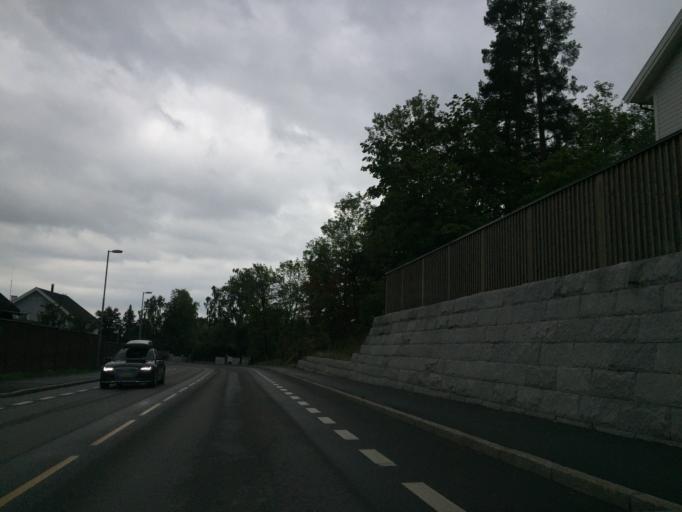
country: NO
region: Oslo
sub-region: Oslo
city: Sjolyststranda
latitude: 59.9482
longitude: 10.6763
